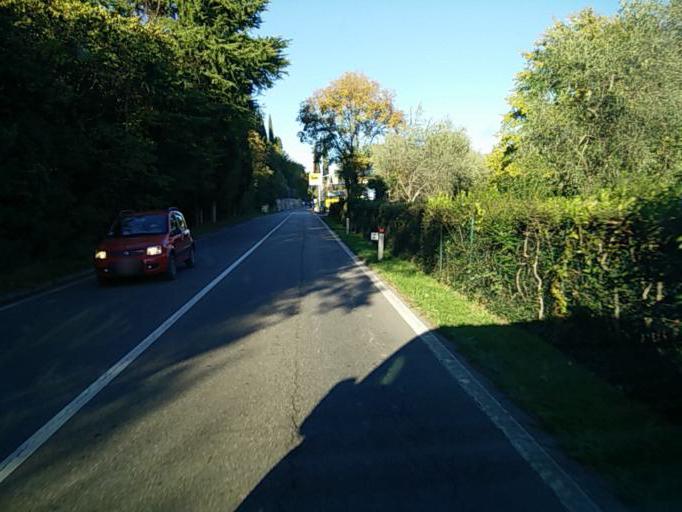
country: IT
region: Lombardy
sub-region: Provincia di Brescia
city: Gargnano
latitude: 45.6616
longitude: 10.6427
